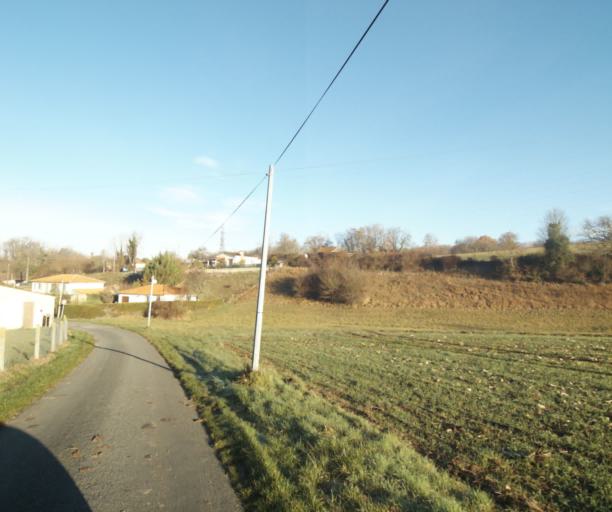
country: FR
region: Poitou-Charentes
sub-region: Departement de la Charente-Maritime
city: Fontcouverte
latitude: 45.7548
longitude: -0.6073
